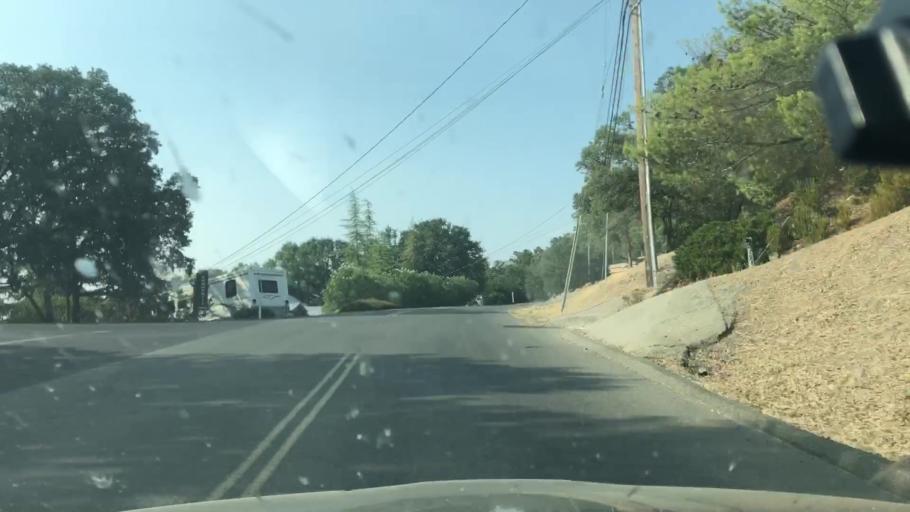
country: US
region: California
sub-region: Lake County
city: Hidden Valley Lake
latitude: 38.8054
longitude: -122.5591
